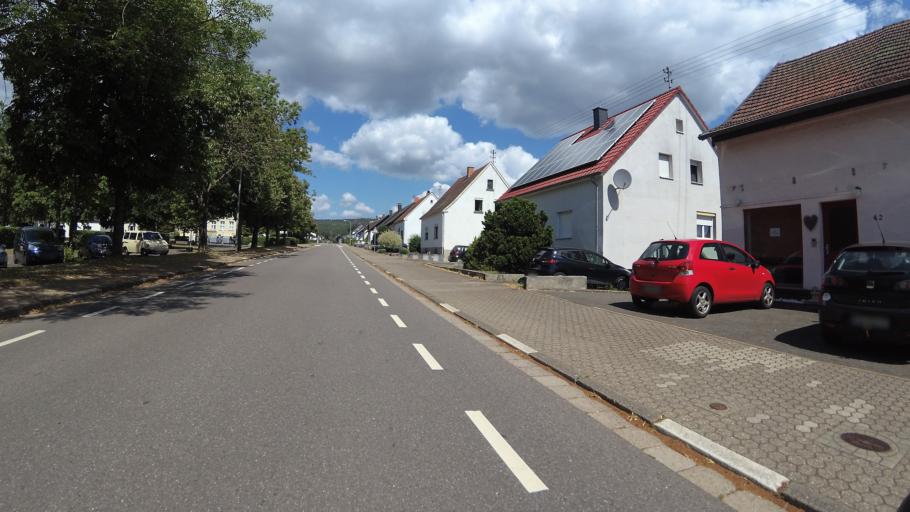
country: DE
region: Saarland
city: Weiskirchen
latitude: 49.5430
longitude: 6.7920
